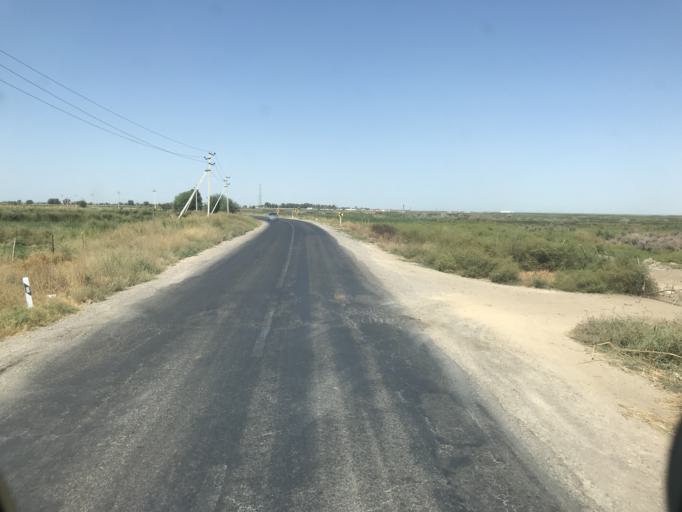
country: KZ
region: Ongtustik Qazaqstan
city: Ilyich
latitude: 40.9506
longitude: 68.4823
